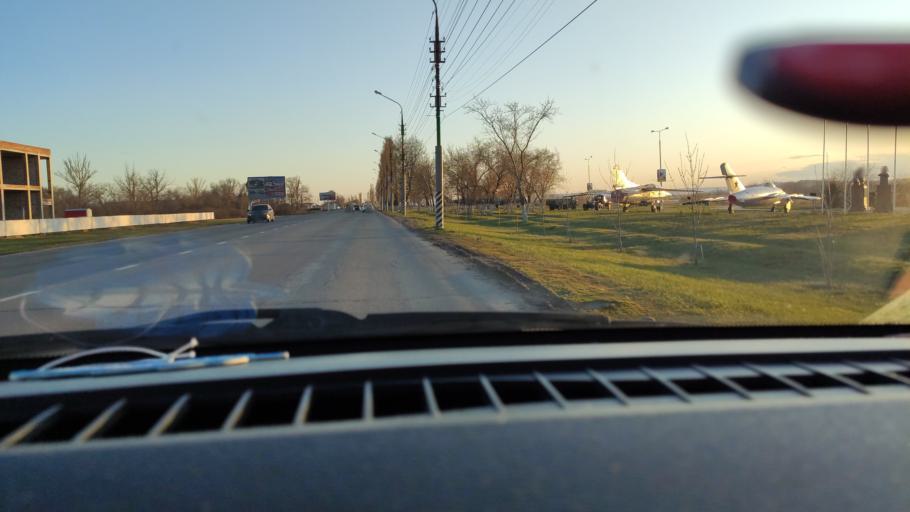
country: RU
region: Saratov
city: Privolzhskiy
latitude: 51.4439
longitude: 46.0719
